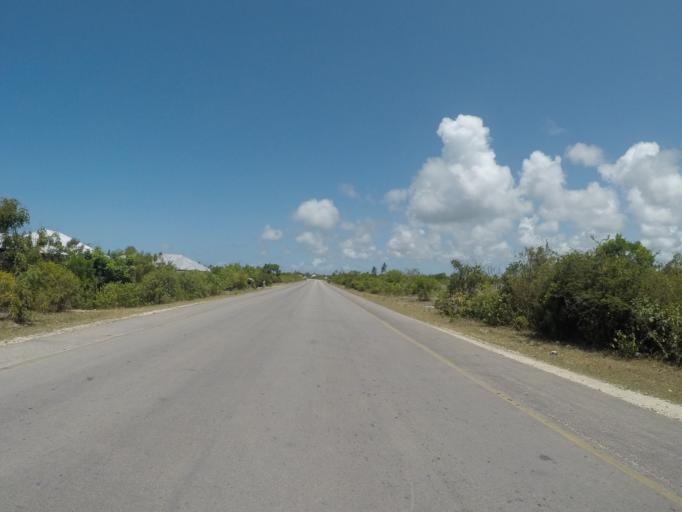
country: TZ
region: Zanzibar Central/South
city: Nganane
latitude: -6.3134
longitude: 39.5418
